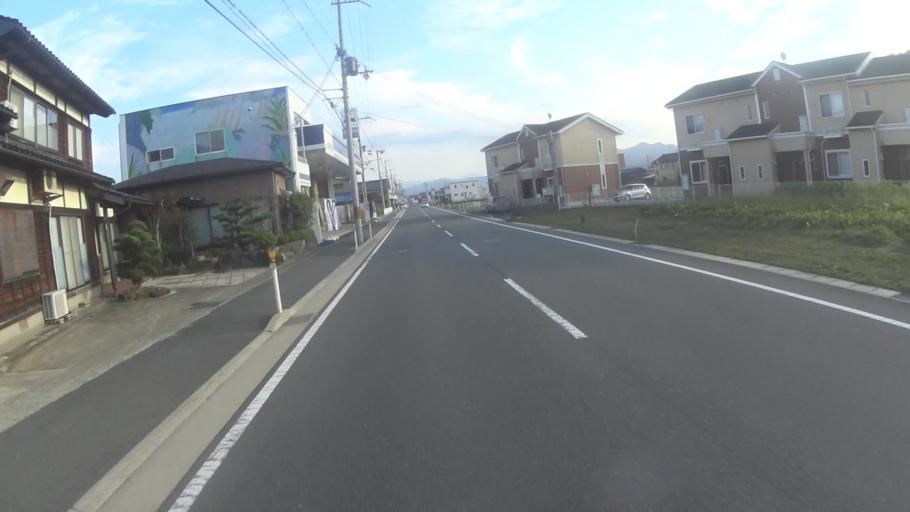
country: JP
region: Kyoto
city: Miyazu
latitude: 35.6251
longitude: 135.0729
